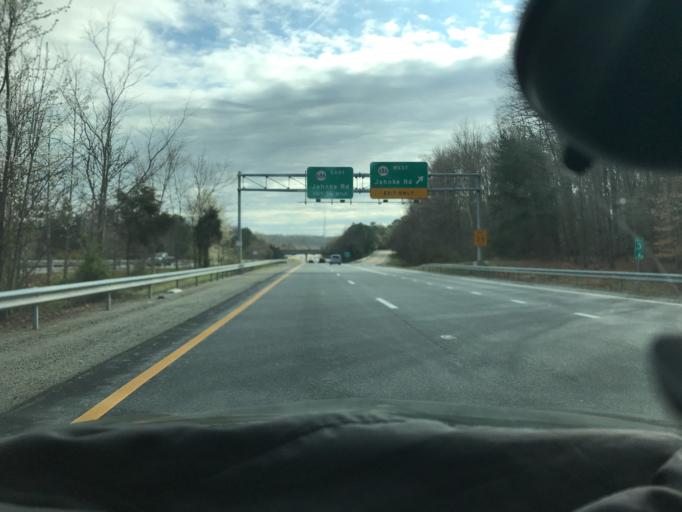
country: US
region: Virginia
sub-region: Chesterfield County
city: Bon Air
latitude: 37.5219
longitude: -77.5331
